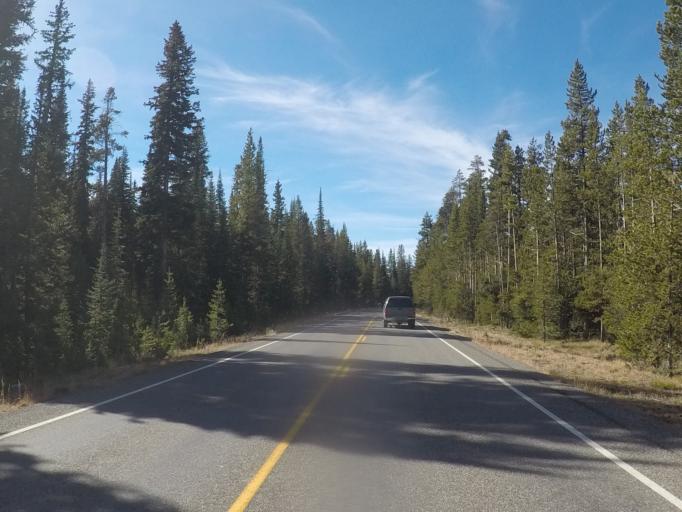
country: US
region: Montana
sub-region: Gallatin County
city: West Yellowstone
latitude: 44.4645
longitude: -110.4750
